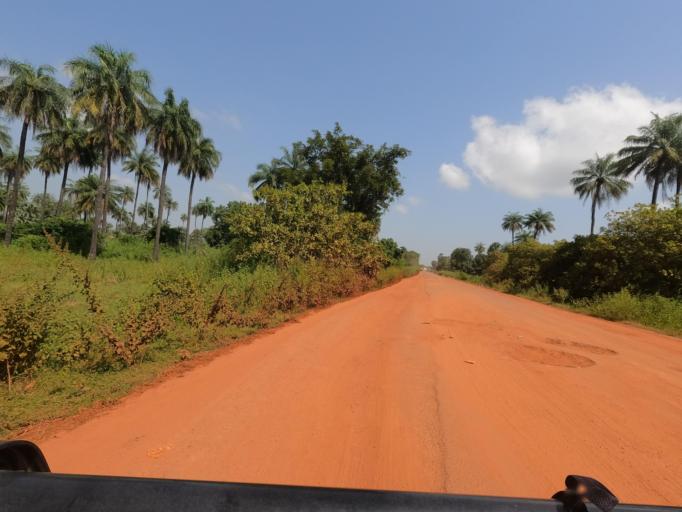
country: GW
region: Cacheu
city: Canchungo
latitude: 12.2775
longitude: -15.7863
